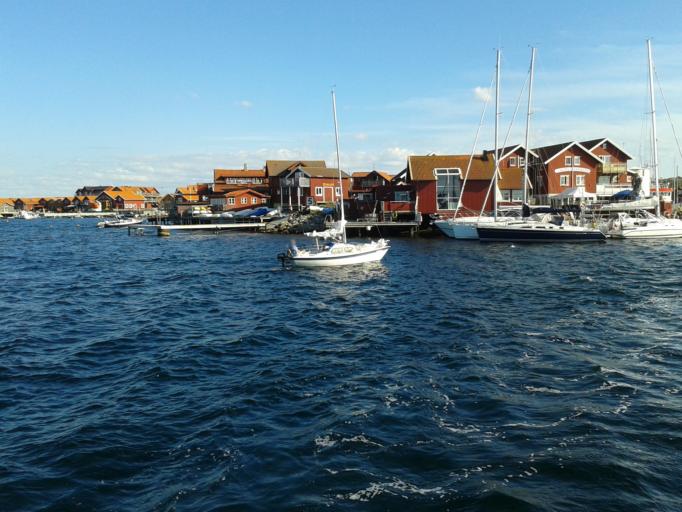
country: SE
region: Vaestra Goetaland
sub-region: Lysekils Kommun
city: Lysekil
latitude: 58.1142
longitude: 11.3667
